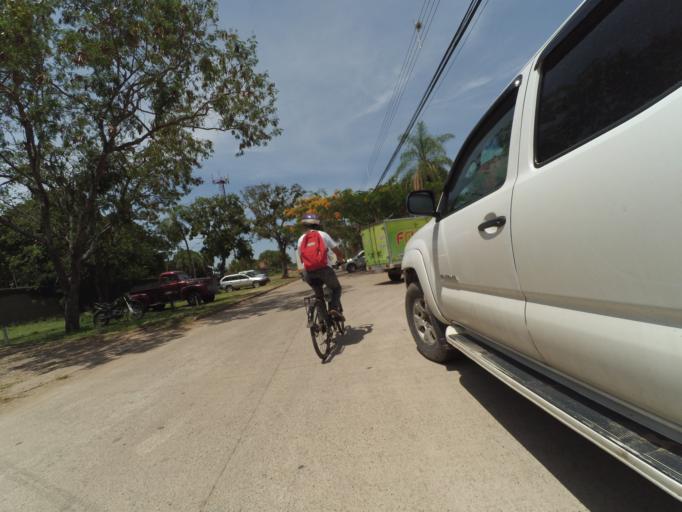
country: BO
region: Santa Cruz
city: Santa Cruz de la Sierra
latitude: -17.8191
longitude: -63.2202
